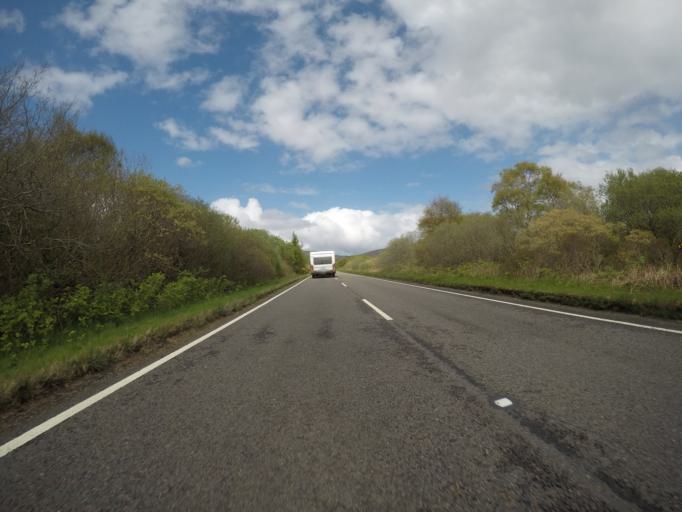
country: GB
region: Scotland
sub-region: Highland
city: Portree
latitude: 57.2535
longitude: -5.9375
